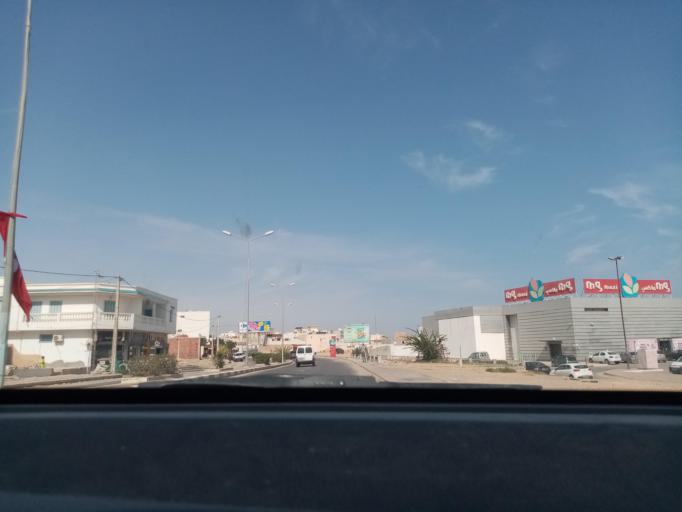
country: TN
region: Qabis
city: Gabes
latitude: 33.8482
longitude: 10.1124
